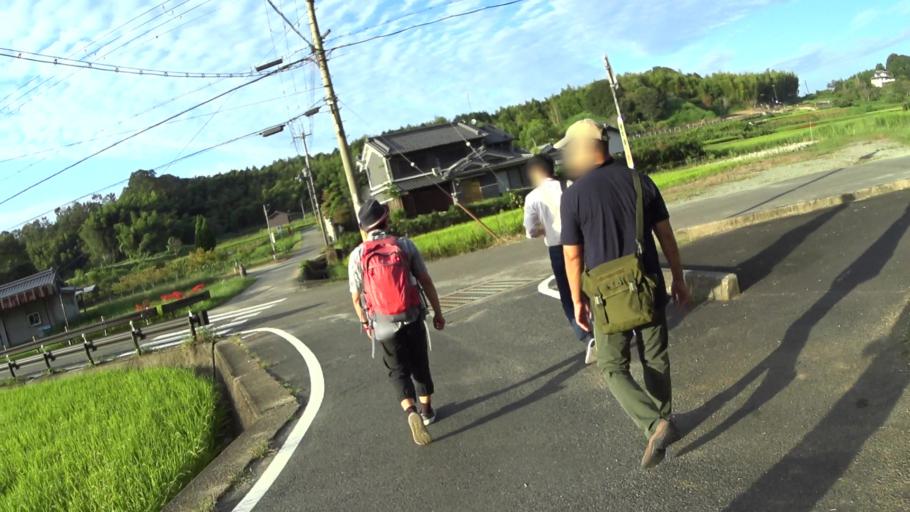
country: JP
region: Nara
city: Kashihara-shi
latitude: 34.4671
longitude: 135.8029
